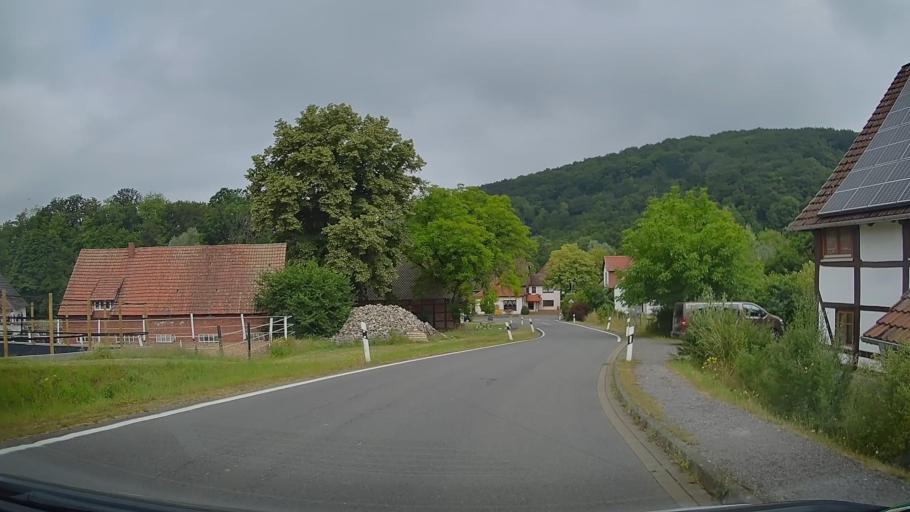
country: DE
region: Lower Saxony
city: Rinteln
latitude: 52.1247
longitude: 9.1083
